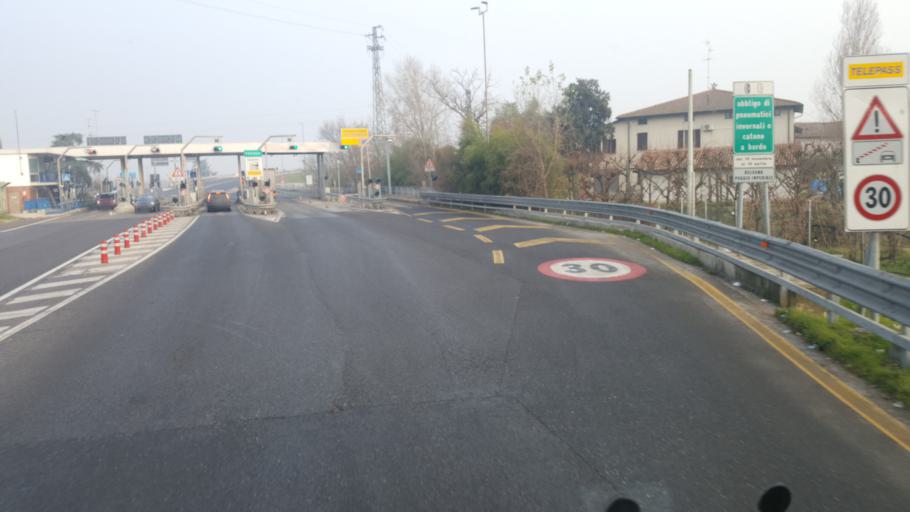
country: IT
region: Emilia-Romagna
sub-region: Provincia di Ravenna
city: Faenza
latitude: 44.3214
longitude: 11.9042
